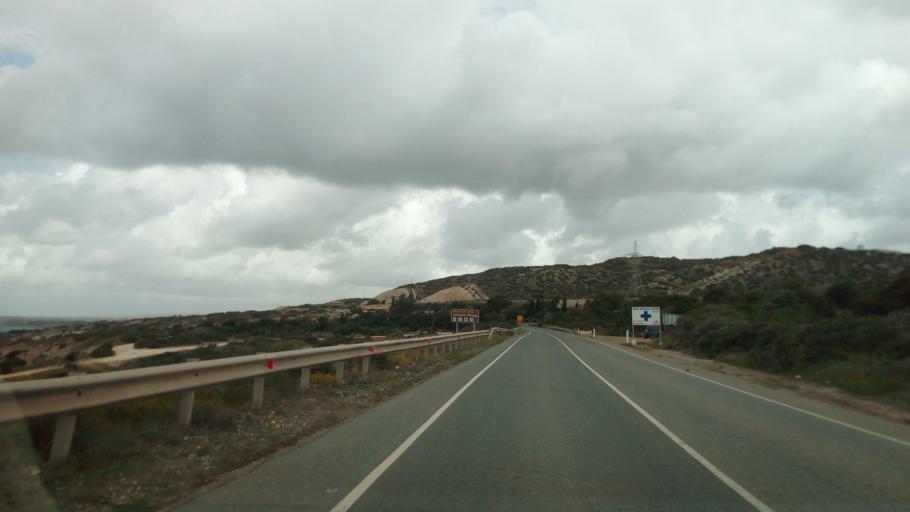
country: CY
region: Limassol
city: Pissouri
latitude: 34.6730
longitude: 32.6078
